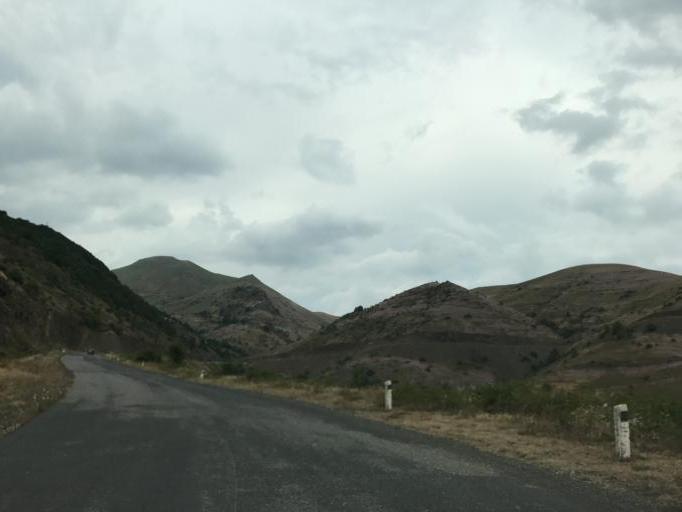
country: AZ
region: Lacin
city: Lacin
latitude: 39.6786
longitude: 46.6360
